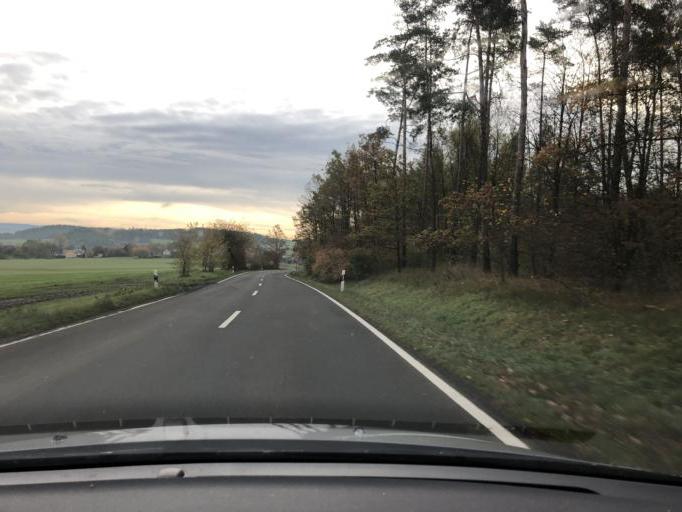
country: DE
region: Thuringia
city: Reurieth
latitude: 50.4099
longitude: 10.6719
